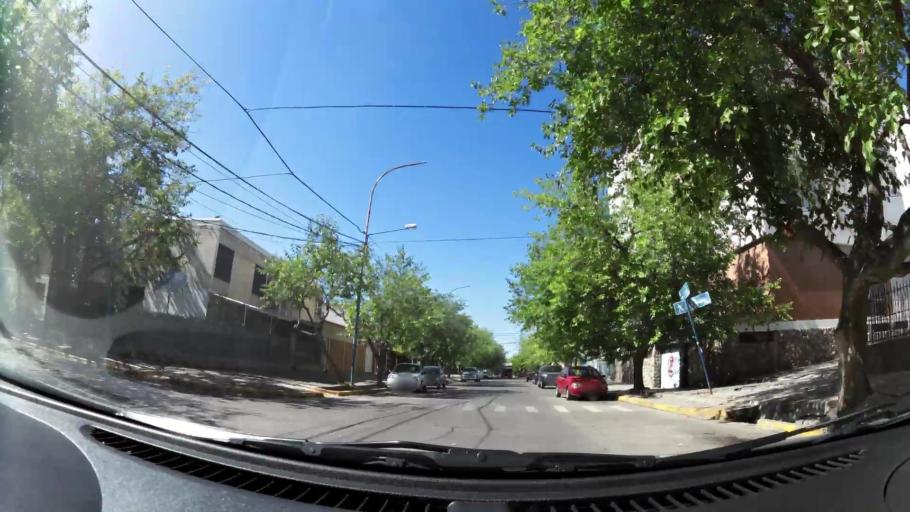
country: AR
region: Mendoza
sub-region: Departamento de Godoy Cruz
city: Godoy Cruz
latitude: -32.9103
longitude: -68.8737
